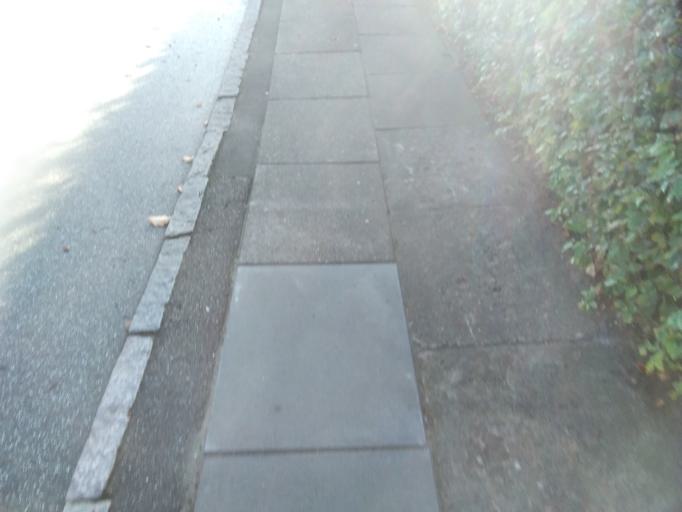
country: DK
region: Capital Region
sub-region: Gladsaxe Municipality
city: Buddinge
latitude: 55.7208
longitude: 12.5094
